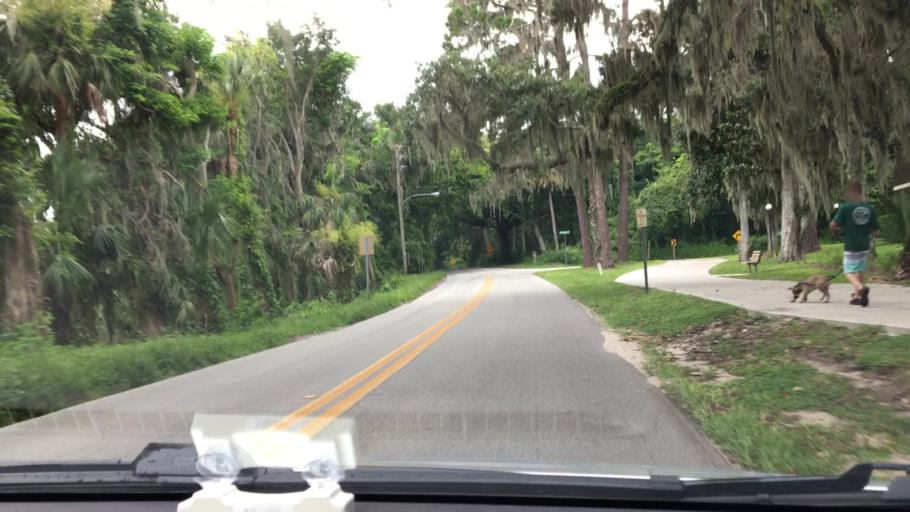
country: US
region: Florida
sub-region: Volusia County
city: Deltona
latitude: 28.8644
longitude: -81.2552
